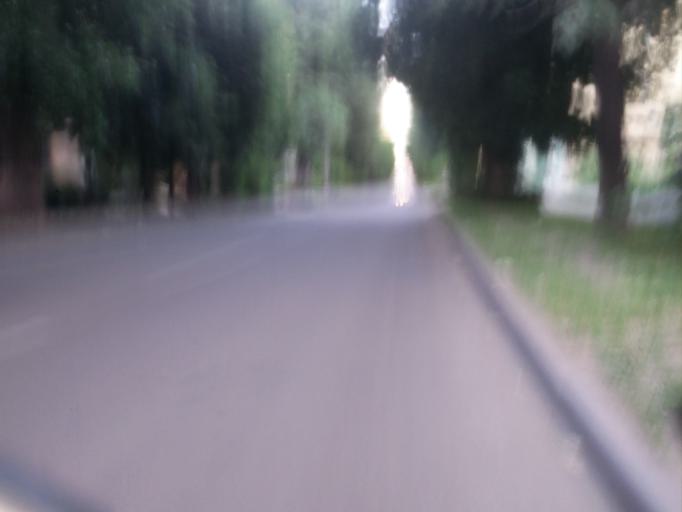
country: RU
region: Voronezj
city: Voronezh
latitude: 51.6518
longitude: 39.1749
